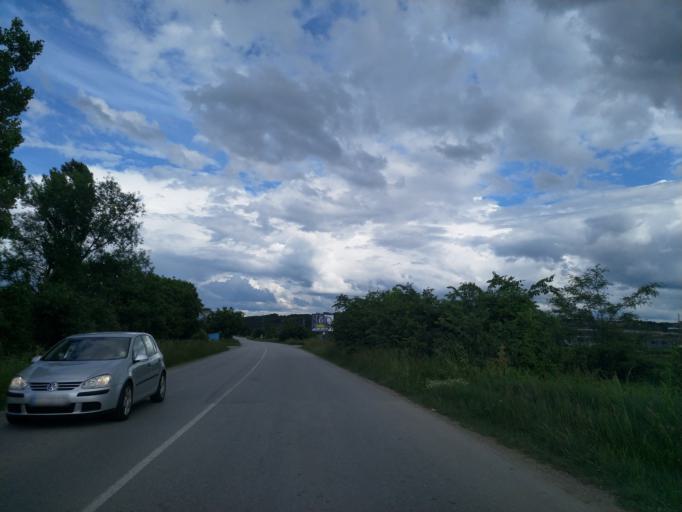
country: RS
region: Central Serbia
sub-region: Pomoravski Okrug
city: Jagodina
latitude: 43.9578
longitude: 21.2901
